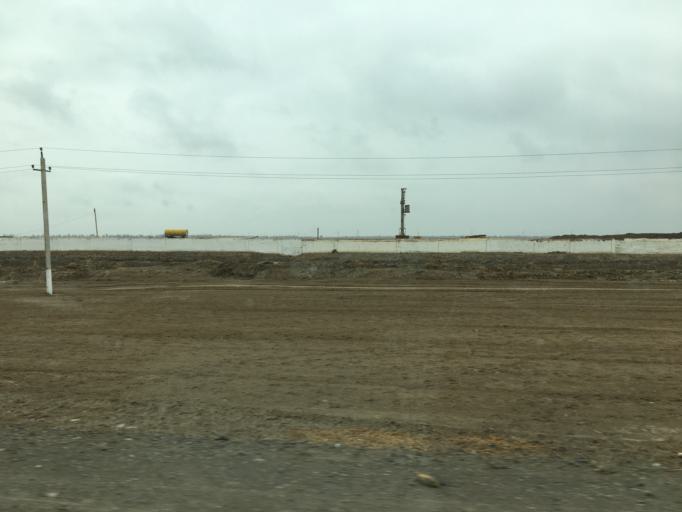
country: TM
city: Murgab
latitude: 37.4795
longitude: 62.0075
